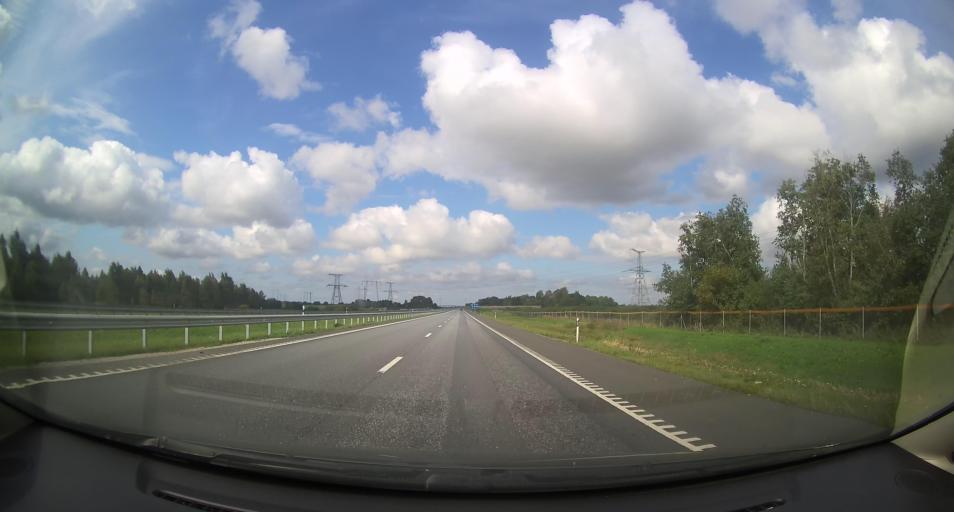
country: EE
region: Harju
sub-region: Rae vald
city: Vaida
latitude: 59.2713
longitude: 24.9905
